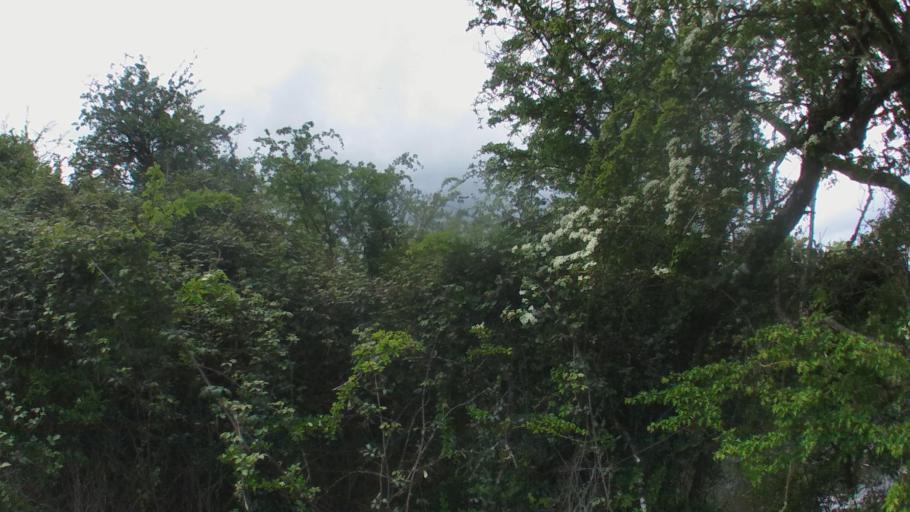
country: IE
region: Leinster
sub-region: Kilkenny
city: Thomastown
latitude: 52.5963
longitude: -7.1846
